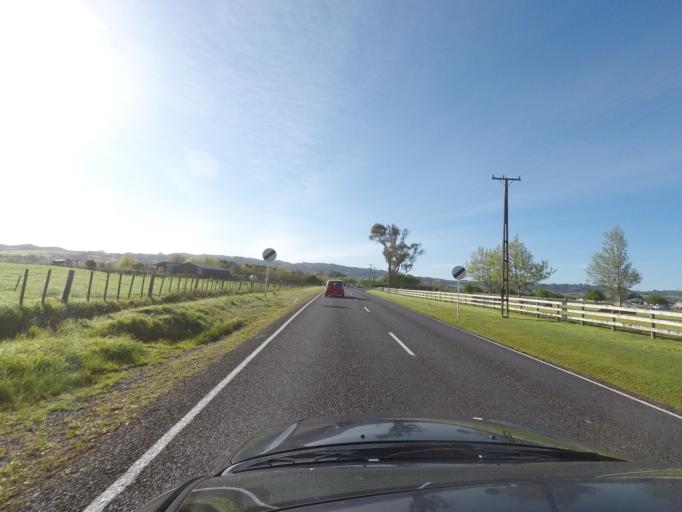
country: NZ
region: Auckland
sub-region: Auckland
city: Red Hill
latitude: -37.0024
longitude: 175.0420
